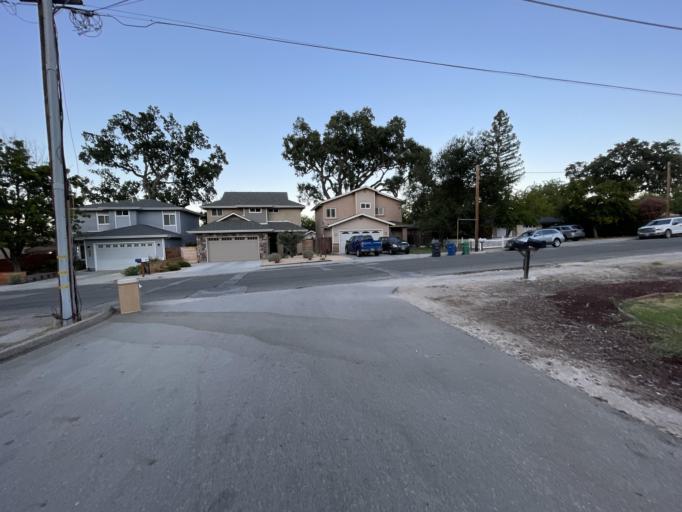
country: US
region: California
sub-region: San Luis Obispo County
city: Paso Robles
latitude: 35.6447
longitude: -120.6957
